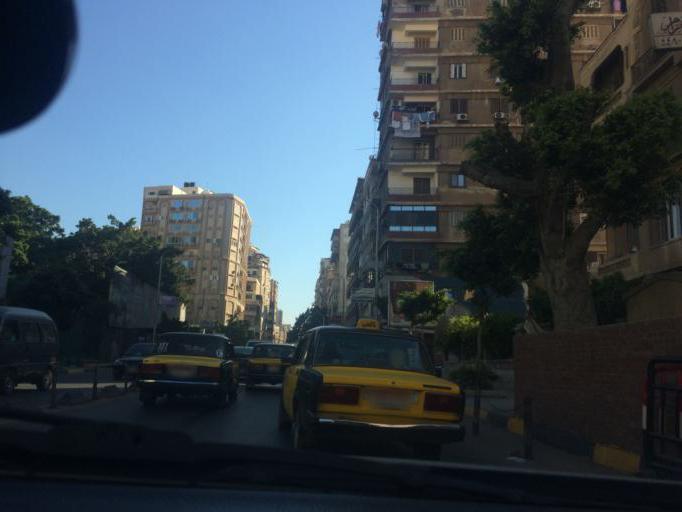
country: EG
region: Alexandria
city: Alexandria
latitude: 31.2357
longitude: 29.9600
